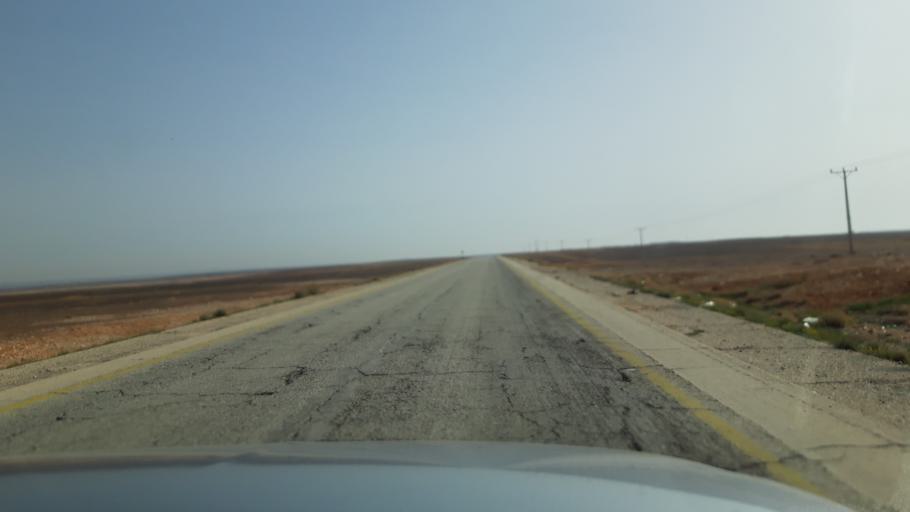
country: JO
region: Amman
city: Al Azraq ash Shamali
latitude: 31.8643
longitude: 36.7092
